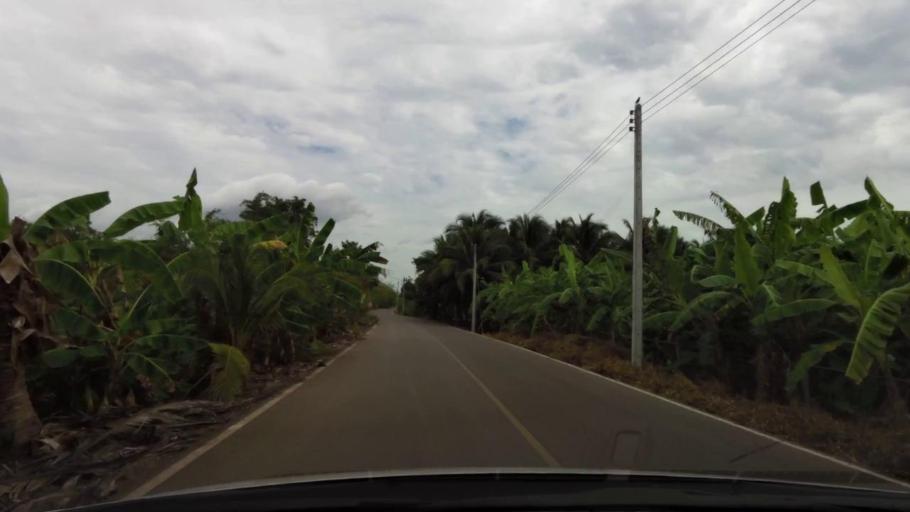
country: TH
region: Ratchaburi
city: Damnoen Saduak
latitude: 13.5530
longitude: 99.9775
